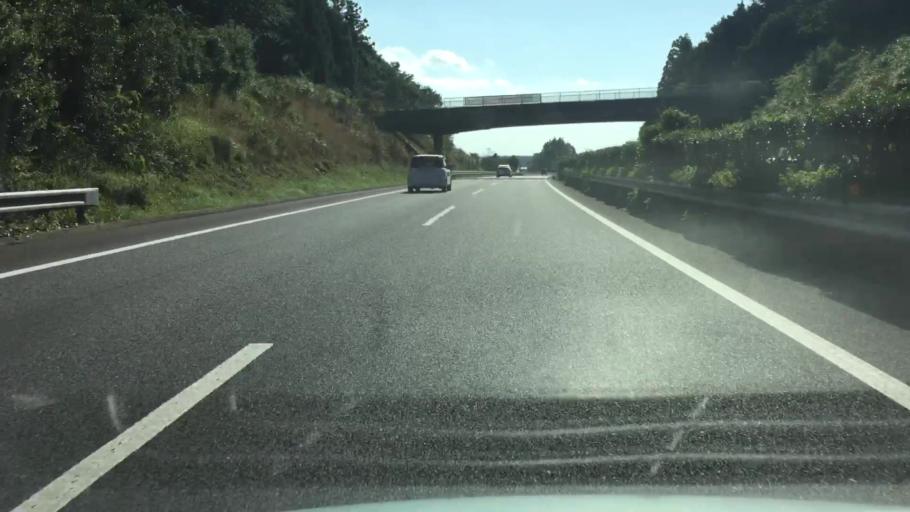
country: JP
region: Ibaraki
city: Tomobe
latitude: 36.3367
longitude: 140.2829
